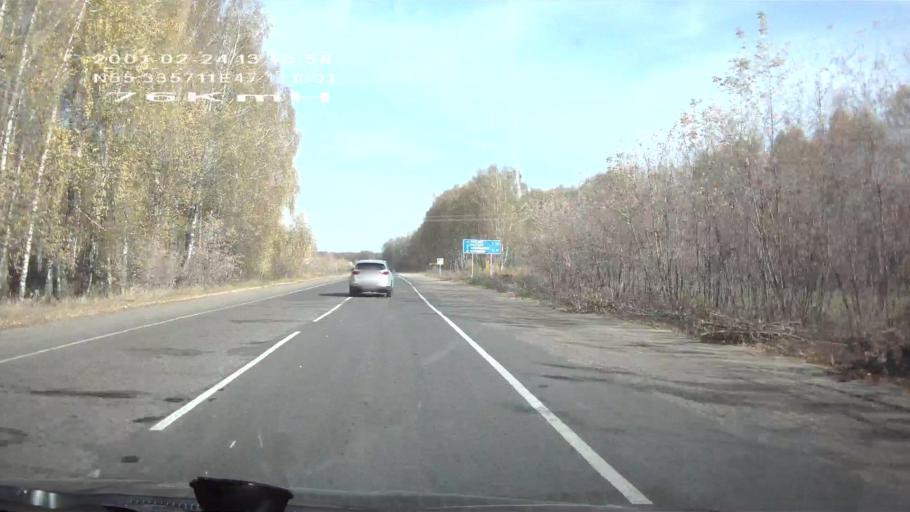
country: RU
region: Chuvashia
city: Ibresi
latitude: 55.3357
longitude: 47.1510
